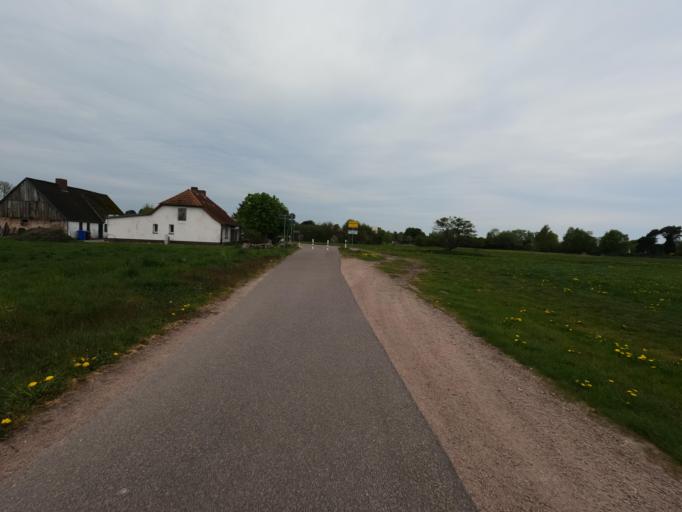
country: DE
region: Mecklenburg-Vorpommern
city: Born
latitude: 54.3439
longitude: 12.5498
